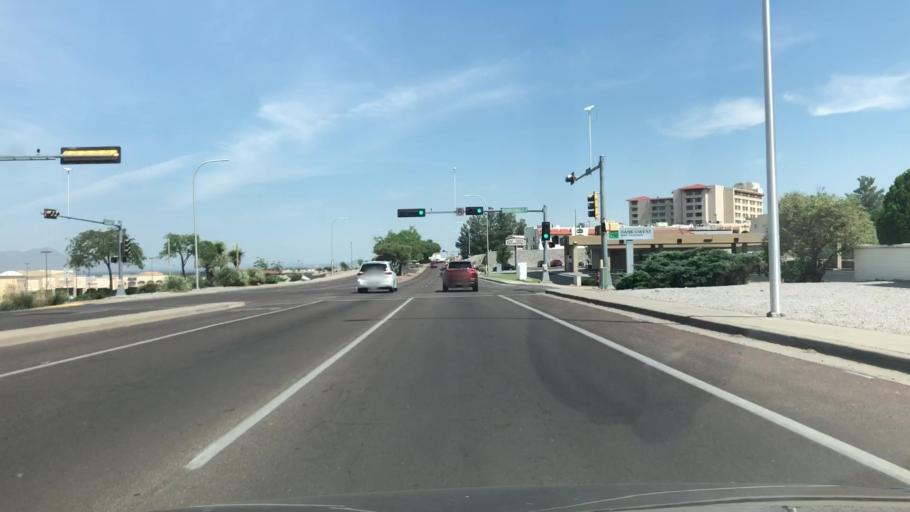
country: US
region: New Mexico
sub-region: Dona Ana County
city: University Park
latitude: 32.3095
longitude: -106.7401
